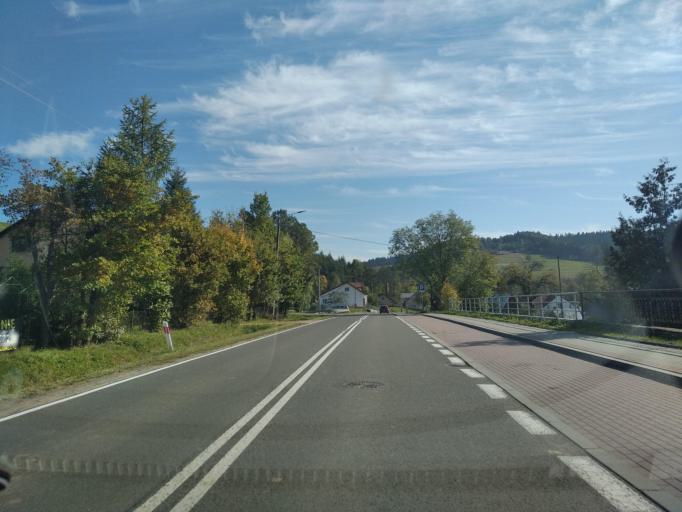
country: PL
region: Subcarpathian Voivodeship
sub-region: Powiat sanocki
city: Komancza
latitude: 49.3391
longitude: 22.0626
